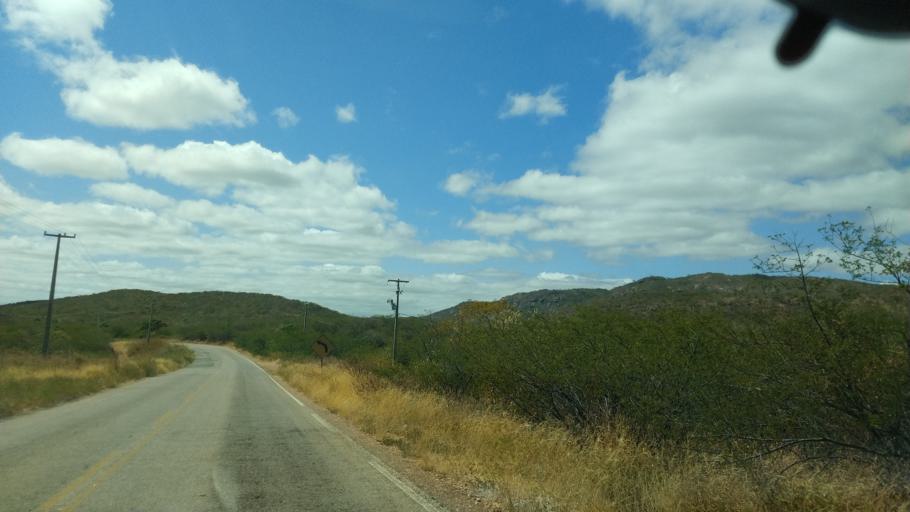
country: BR
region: Rio Grande do Norte
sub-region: Currais Novos
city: Currais Novos
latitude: -6.2643
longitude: -36.5914
